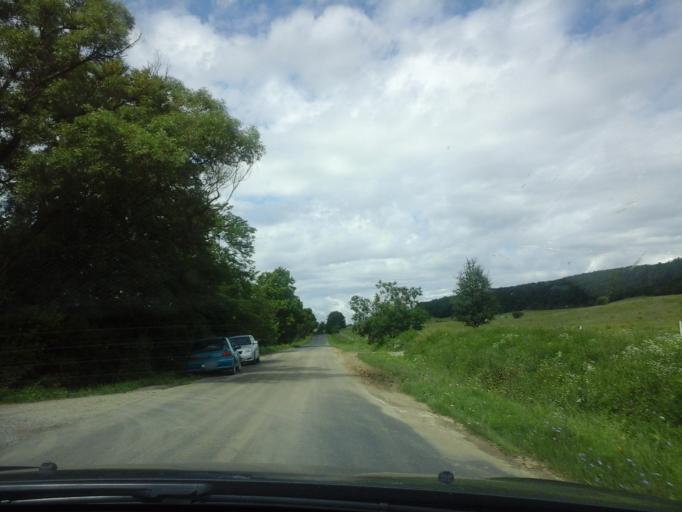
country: HU
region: Borsod-Abauj-Zemplen
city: Rudabanya
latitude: 48.3900
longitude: 20.5483
